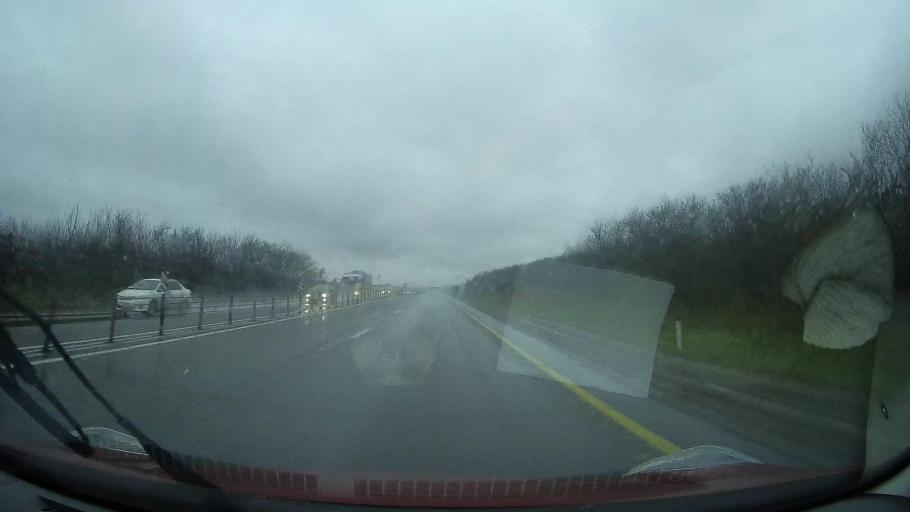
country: RU
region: Stavropol'skiy
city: Nevinnomyssk
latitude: 44.6391
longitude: 41.9779
